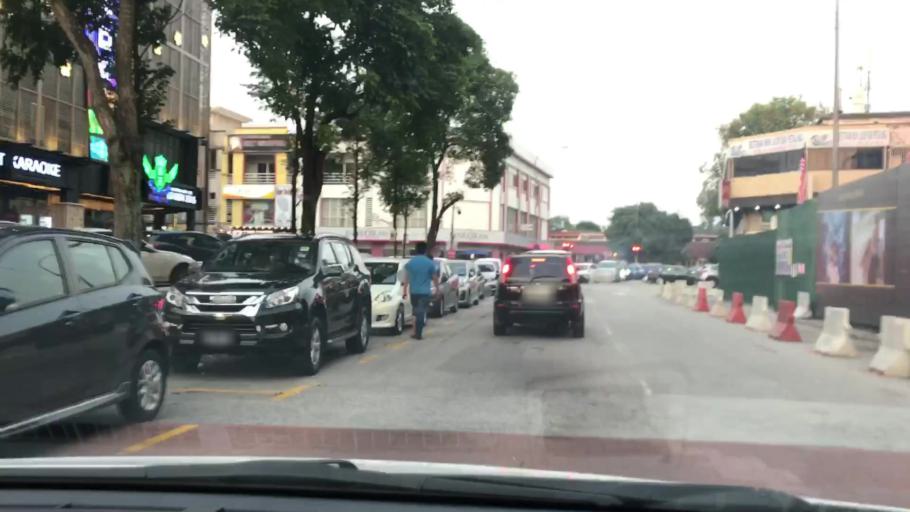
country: MY
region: Selangor
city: Kampong Baharu Balakong
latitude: 3.0684
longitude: 101.6940
